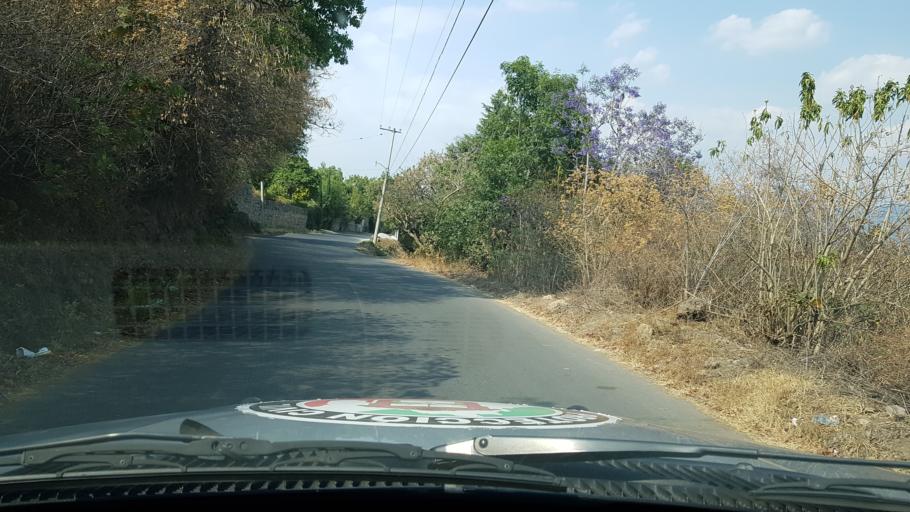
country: MX
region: Mexico
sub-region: Atlautla
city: San Andres Tlalamac
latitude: 18.9737
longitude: -98.8149
